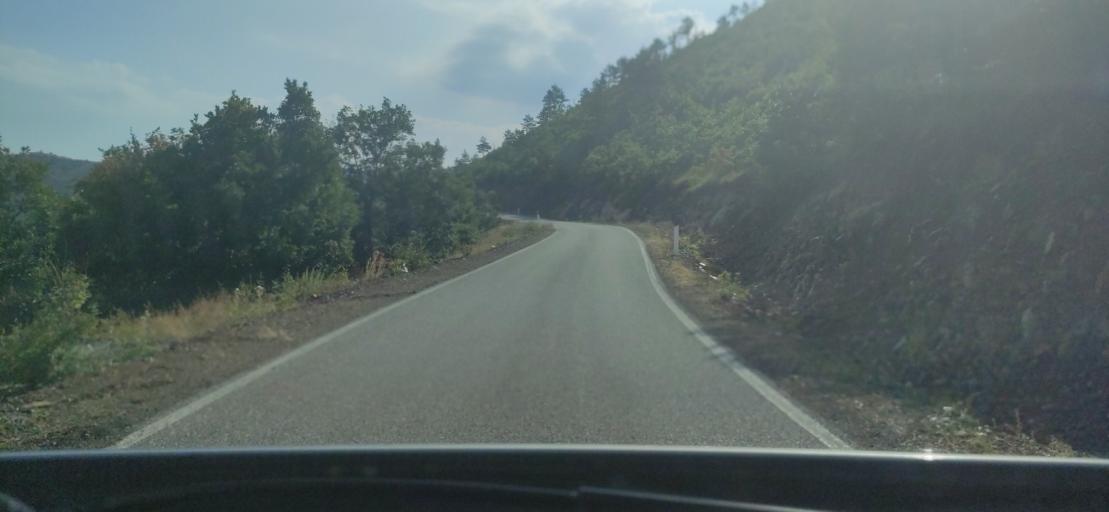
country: AL
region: Shkoder
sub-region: Rrethi i Pukes
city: Iballe
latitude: 42.1695
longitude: 20.0097
